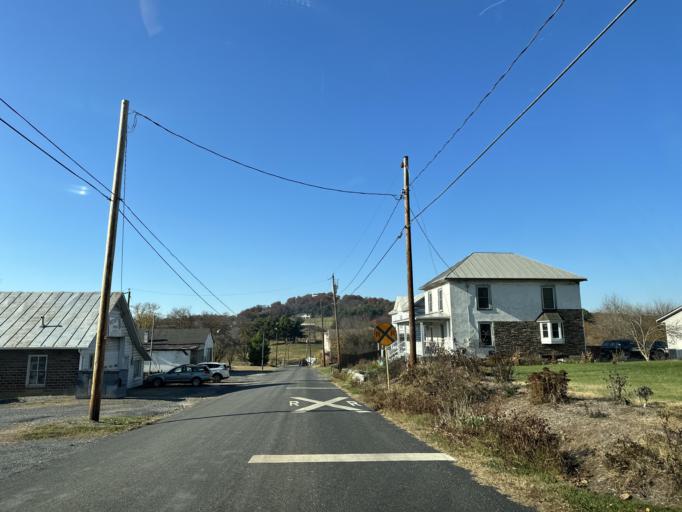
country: US
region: Virginia
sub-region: Augusta County
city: Weyers Cave
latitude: 38.2887
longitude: -78.9109
